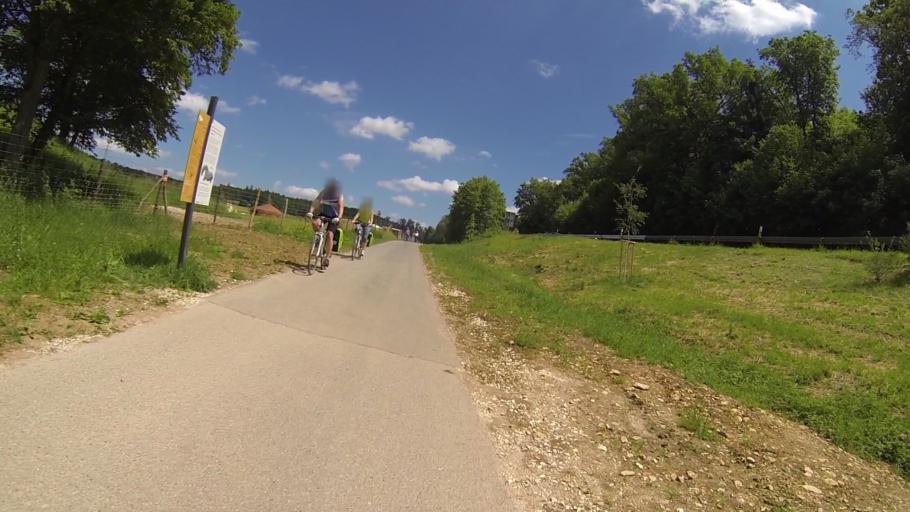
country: DE
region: Baden-Wuerttemberg
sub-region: Tuebingen Region
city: Asselfingen
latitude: 48.5582
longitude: 10.1943
